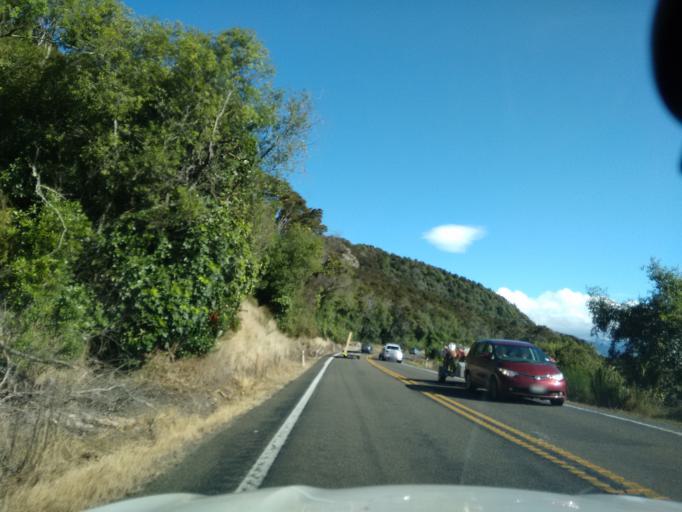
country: NZ
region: Waikato
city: Turangi
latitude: -38.9403
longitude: 175.8583
